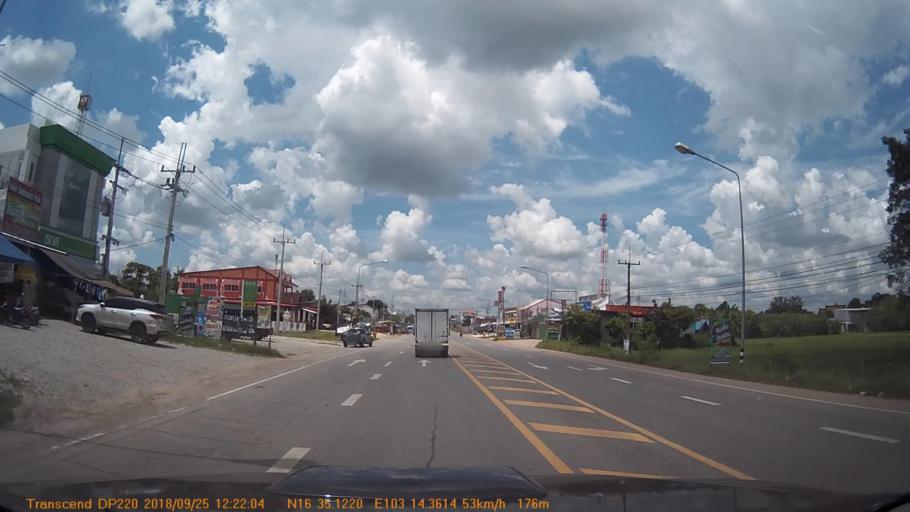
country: TH
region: Kalasin
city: Huai Mek
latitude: 16.5854
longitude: 103.2393
